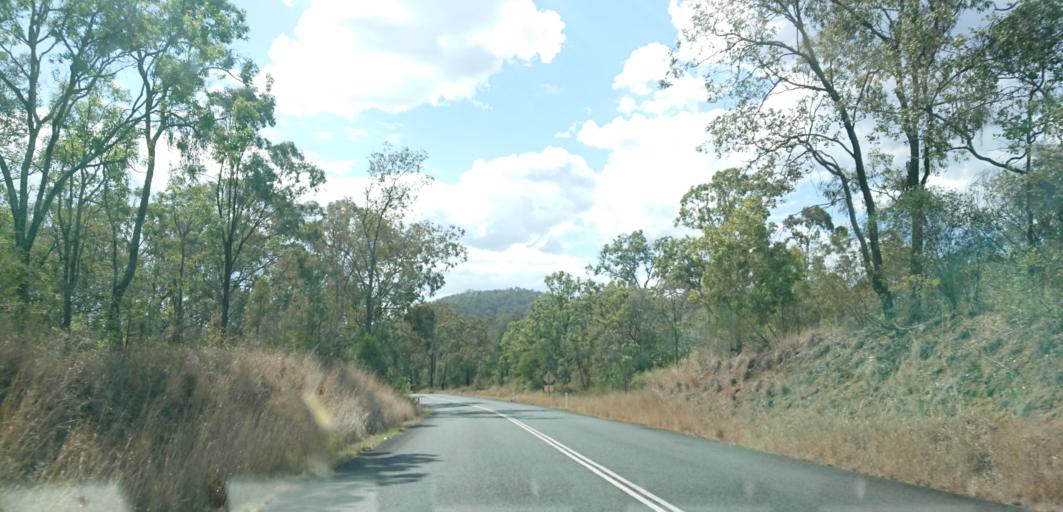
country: AU
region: Queensland
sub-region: Toowoomba
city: Top Camp
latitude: -27.8108
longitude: 152.1065
